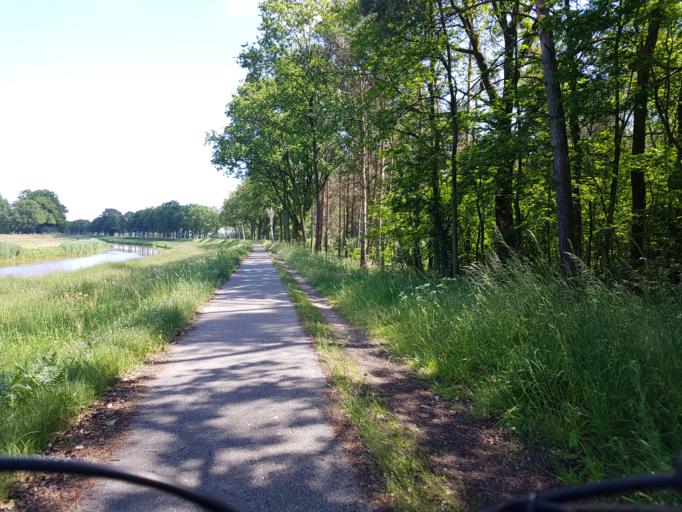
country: DE
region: Brandenburg
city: Bad Liebenwerda
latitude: 51.4839
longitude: 13.4371
